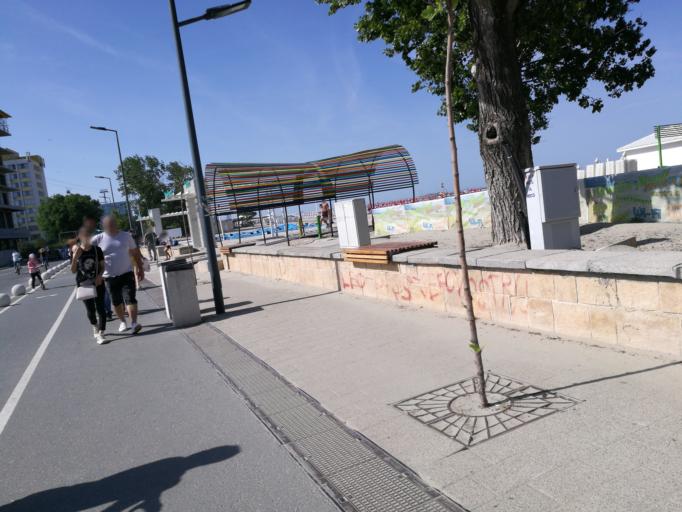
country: RO
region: Constanta
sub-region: Municipiul Constanta
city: Palazu Mare
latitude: 44.2274
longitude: 28.6296
